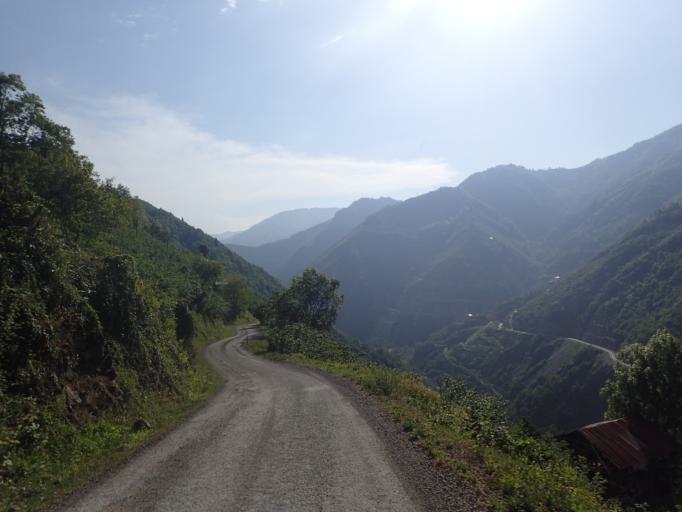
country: TR
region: Ordu
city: Topcam
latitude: 40.7105
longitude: 37.8589
